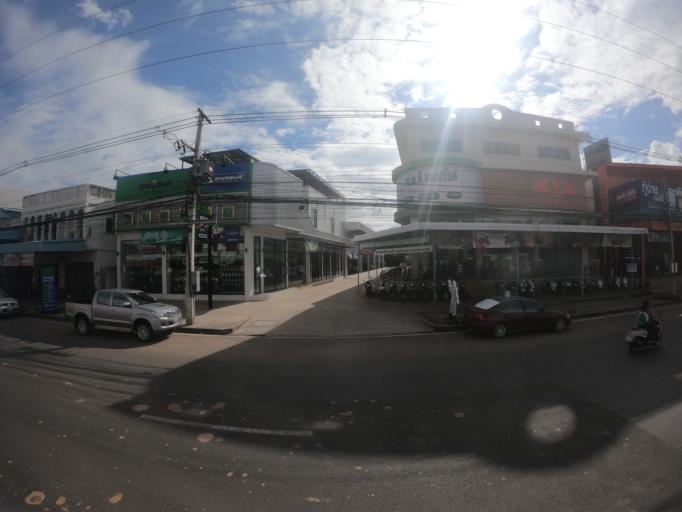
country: TH
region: Surin
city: Prasat
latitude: 14.6341
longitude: 103.4073
